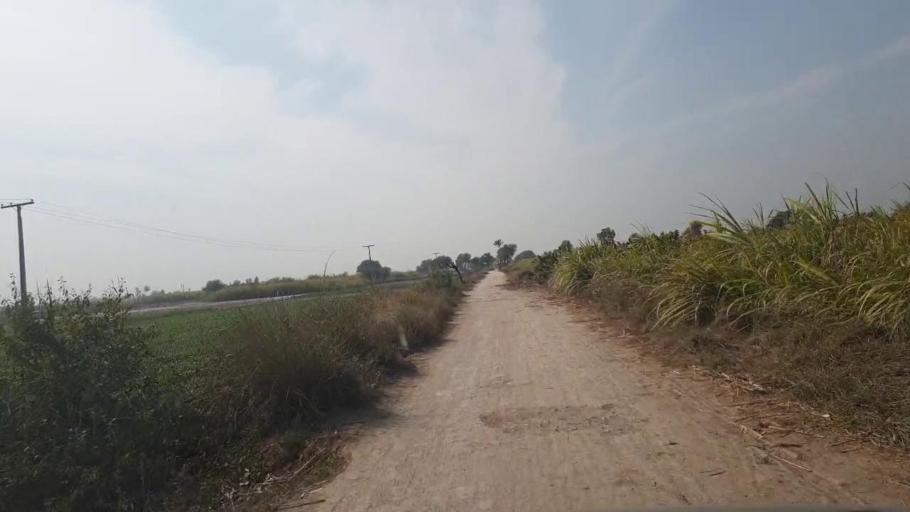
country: PK
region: Sindh
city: Shahdadpur
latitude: 25.8769
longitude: 68.6014
